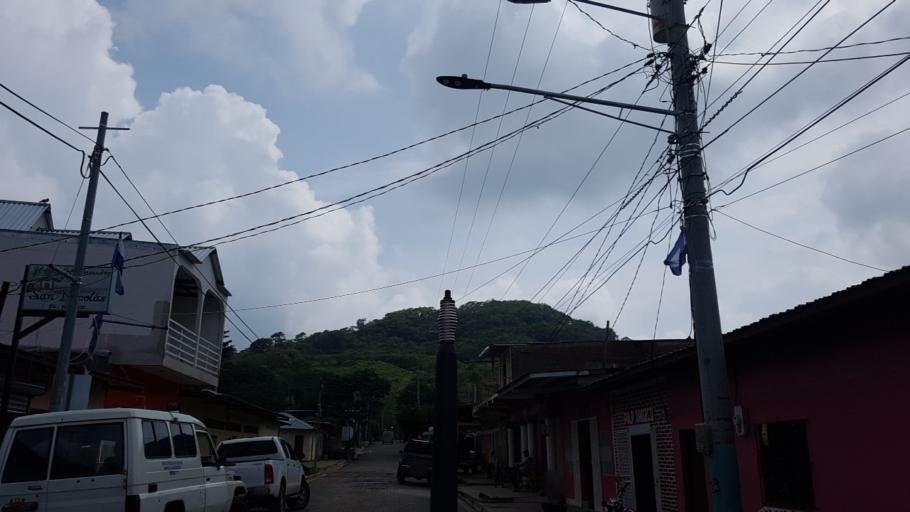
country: NI
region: Leon
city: Santa Rosa del Penon
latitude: 12.9328
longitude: -86.3480
